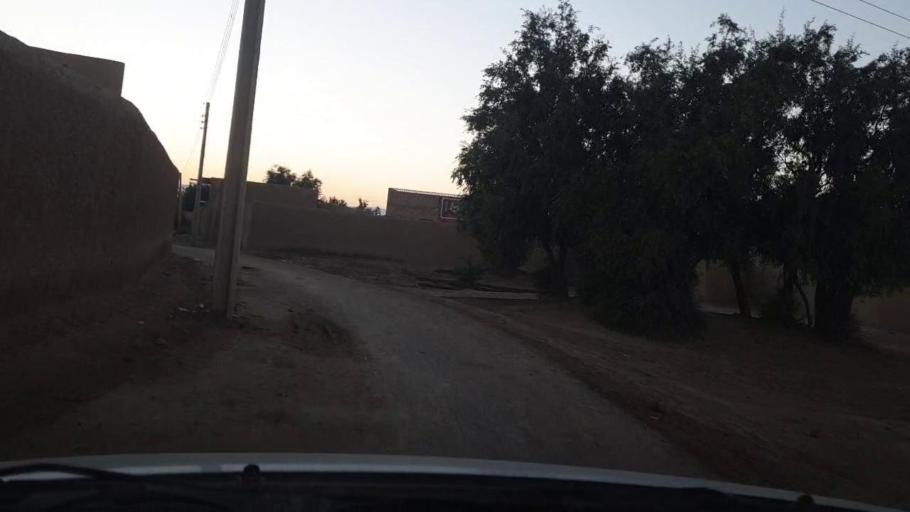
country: PK
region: Sindh
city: Johi
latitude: 26.8349
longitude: 67.4724
